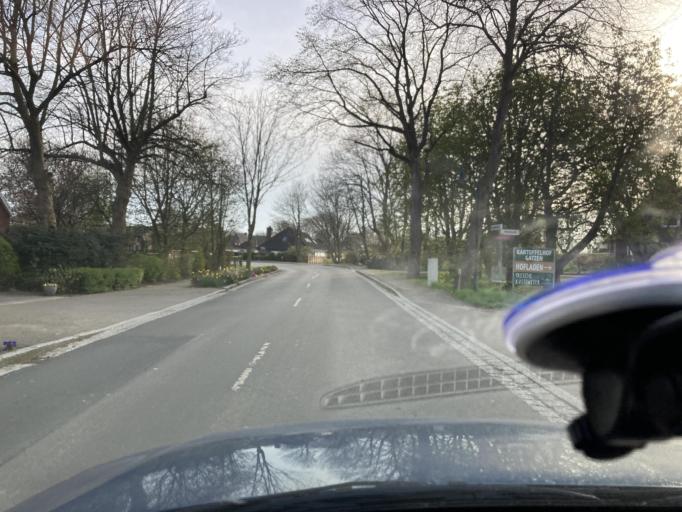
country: DE
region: Schleswig-Holstein
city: Schulp
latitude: 54.2459
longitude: 8.9381
